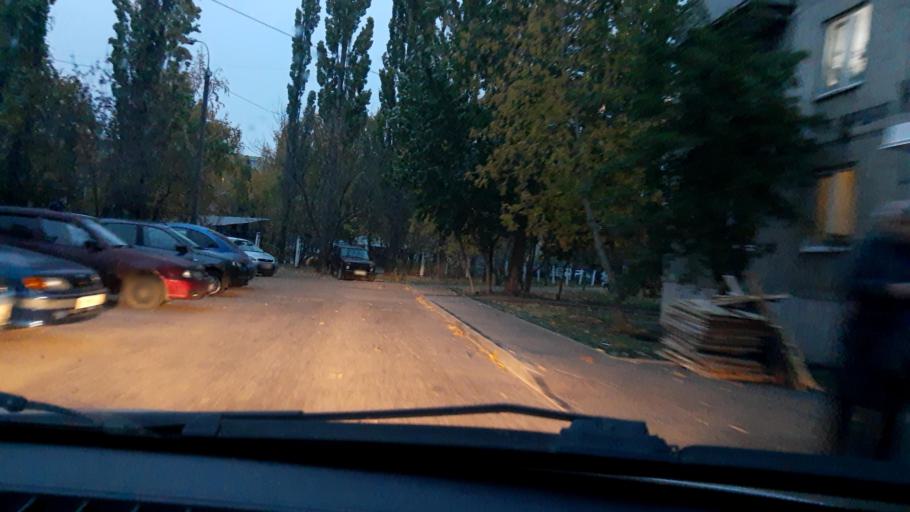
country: RU
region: Bashkortostan
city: Ufa
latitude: 54.7691
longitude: 56.0516
